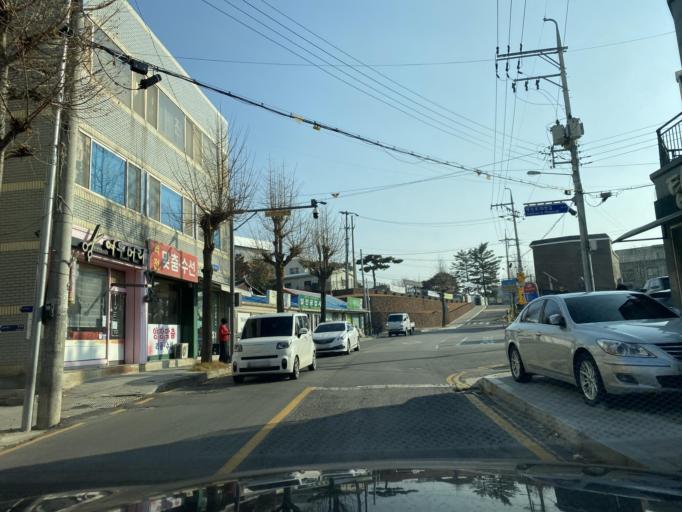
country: KR
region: Chungcheongnam-do
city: Yesan
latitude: 36.6857
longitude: 126.8325
